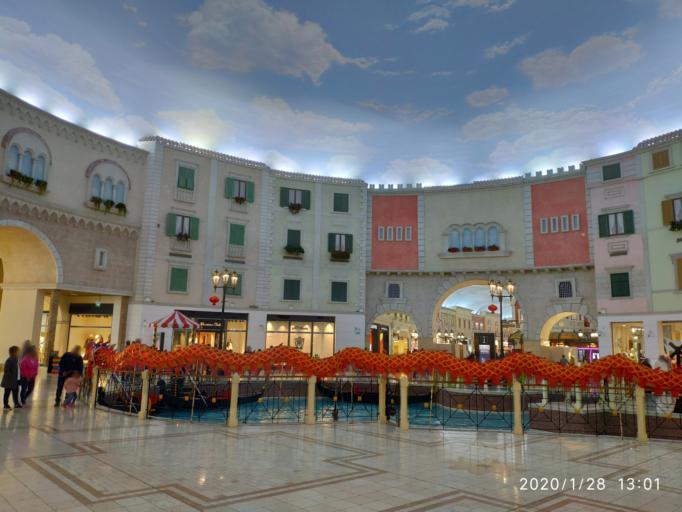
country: QA
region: Baladiyat ar Rayyan
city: Ar Rayyan
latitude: 25.2595
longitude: 51.4439
